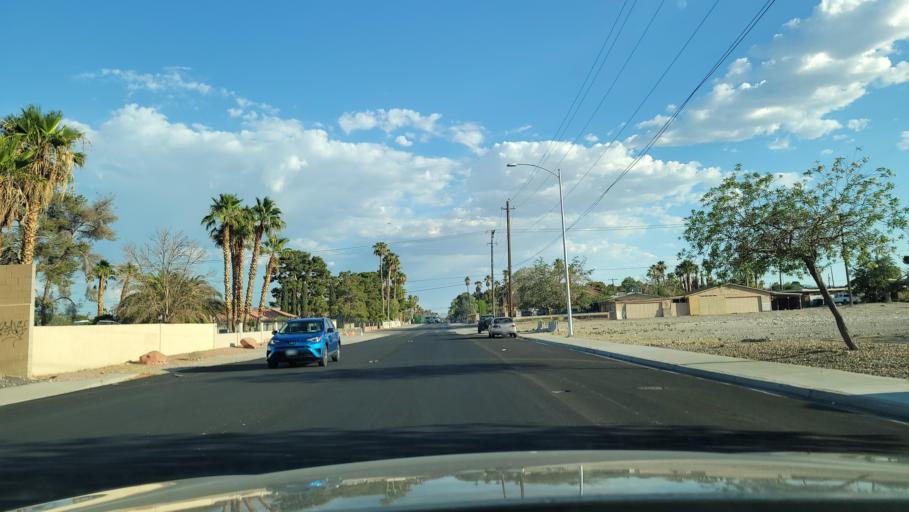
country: US
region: Nevada
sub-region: Clark County
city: Spring Valley
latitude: 36.1583
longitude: -115.2191
